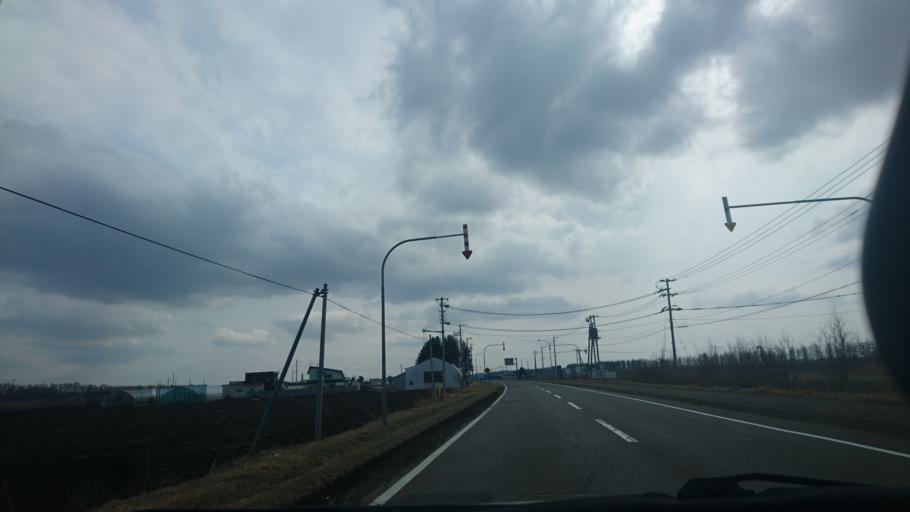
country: JP
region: Hokkaido
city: Otofuke
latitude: 43.2086
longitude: 143.2762
